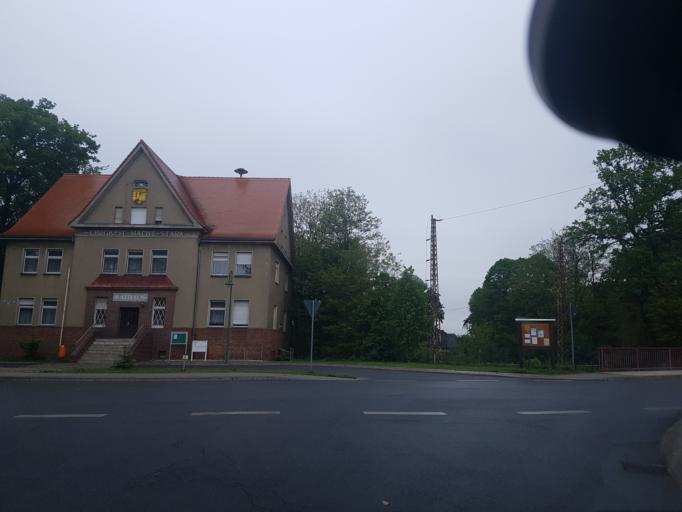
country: DE
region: Brandenburg
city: Neupetershain
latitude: 51.6087
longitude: 14.1655
